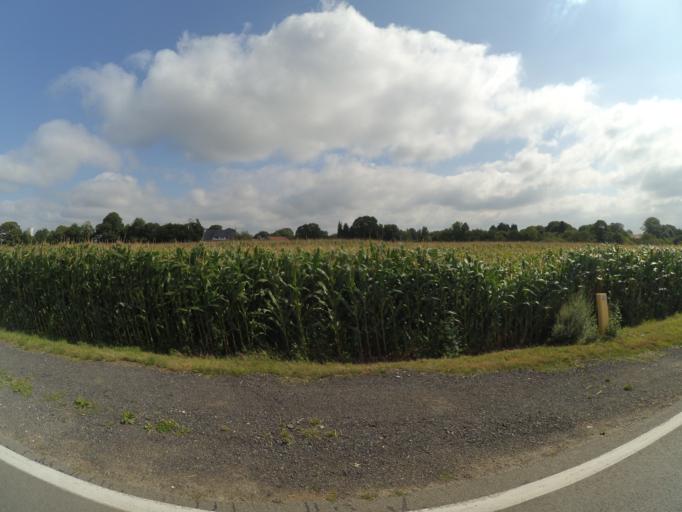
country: FR
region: Brittany
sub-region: Departement du Finistere
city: Mellac
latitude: 47.8967
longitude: -3.5752
